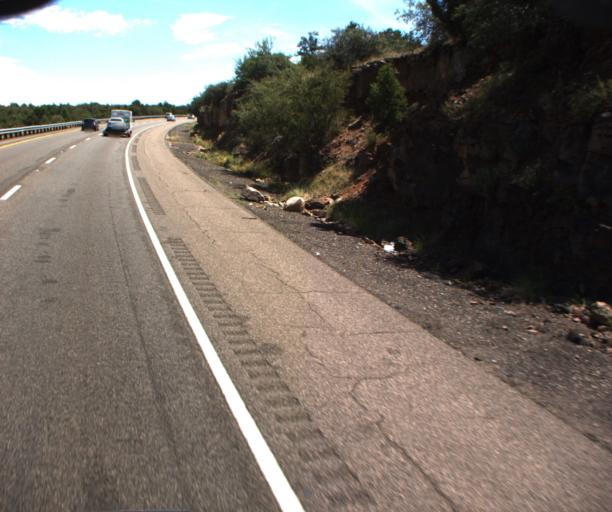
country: US
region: Arizona
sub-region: Yavapai County
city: Village of Oak Creek (Big Park)
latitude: 34.7725
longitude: -111.6374
